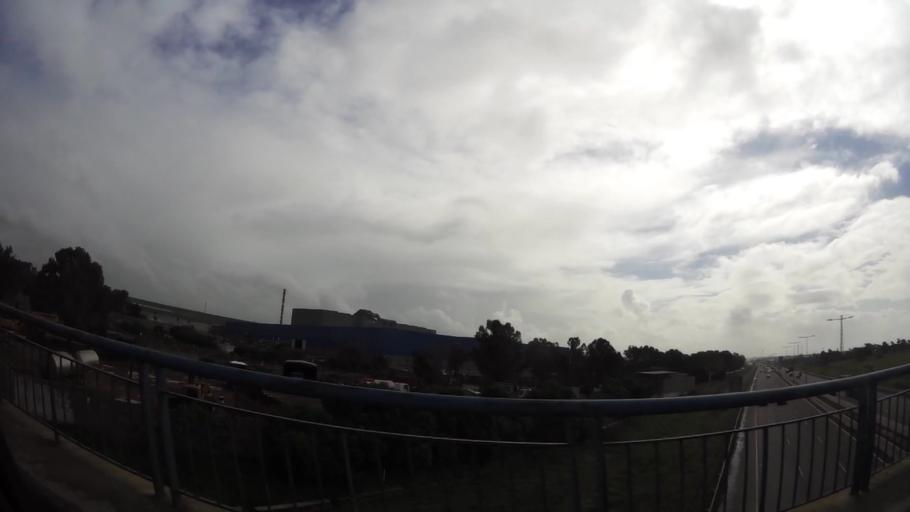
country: MA
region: Grand Casablanca
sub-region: Mohammedia
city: Mohammedia
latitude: 33.6408
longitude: -7.4343
